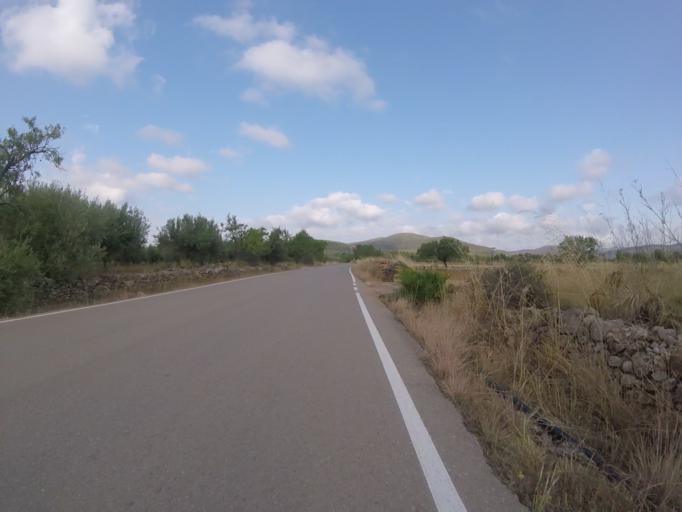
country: ES
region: Valencia
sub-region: Provincia de Castello
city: Santa Magdalena de Pulpis
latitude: 40.3603
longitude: 0.2909
